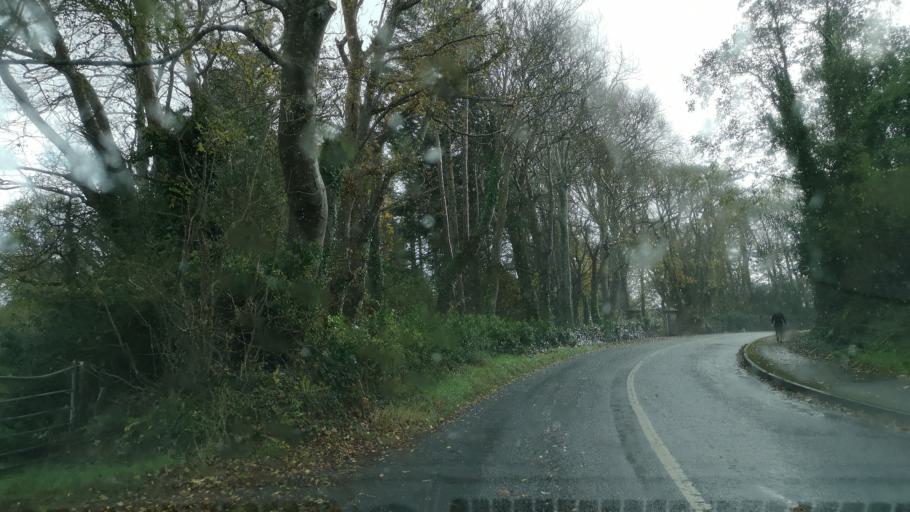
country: IE
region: Connaught
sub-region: Maigh Eo
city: Westport
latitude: 53.7908
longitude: -9.5677
